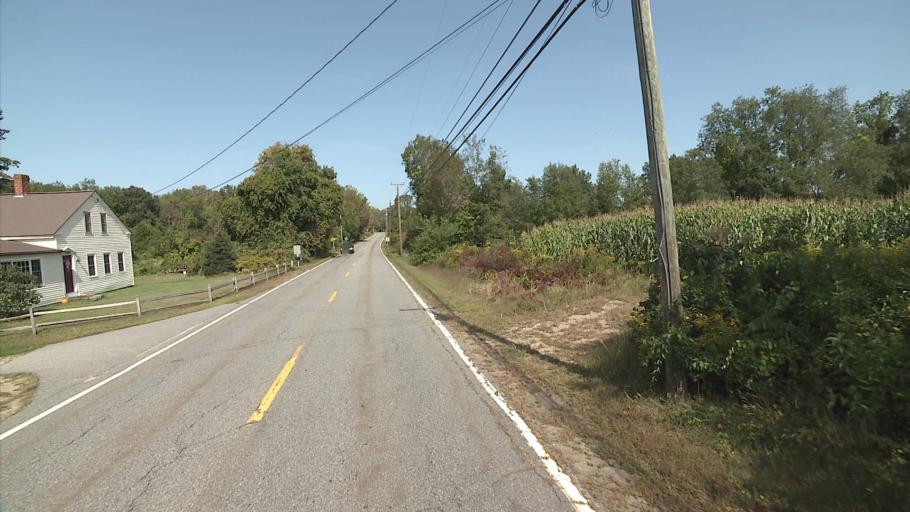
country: US
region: Connecticut
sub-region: Windham County
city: South Woodstock
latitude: 41.9630
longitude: -71.9843
